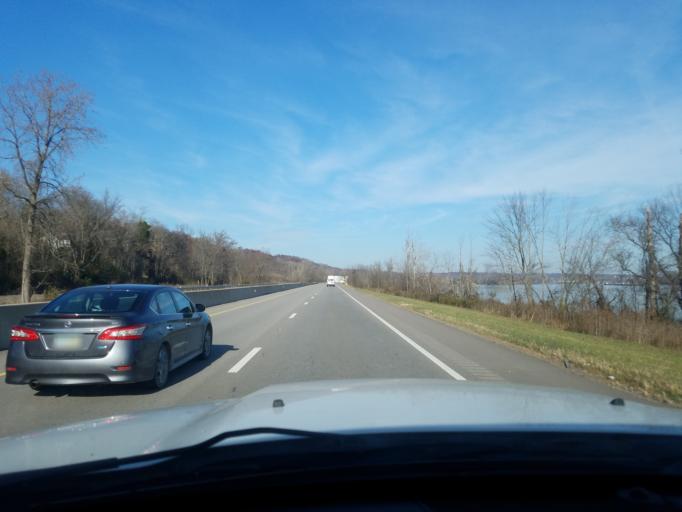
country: US
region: West Virginia
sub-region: Wood County
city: Vienna
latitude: 39.3361
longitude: -81.5604
